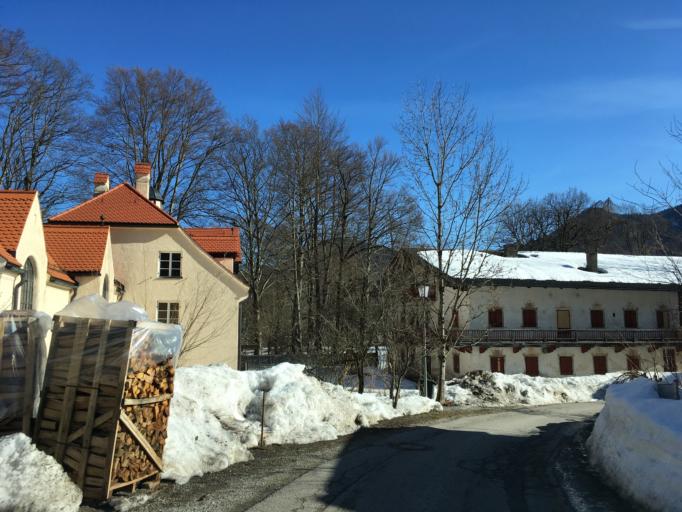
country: DE
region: Bavaria
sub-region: Upper Bavaria
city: Aschau im Chiemgau
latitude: 47.7631
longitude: 12.3118
